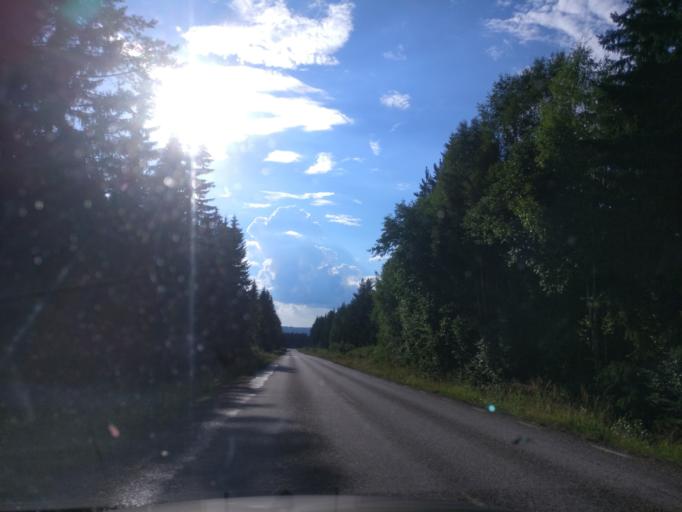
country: SE
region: Dalarna
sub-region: Ludvika Kommun
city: Ludvika
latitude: 60.2653
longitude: 15.0426
